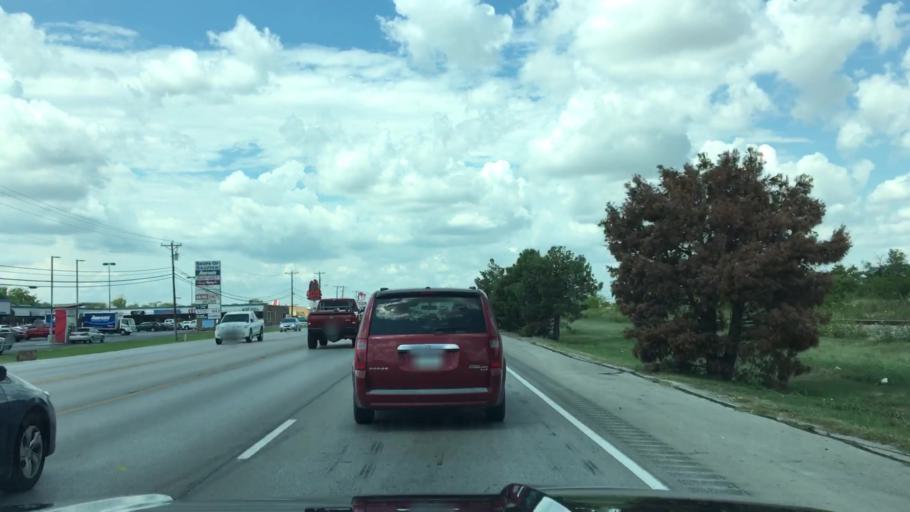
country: US
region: Texas
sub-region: Tarrant County
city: Saginaw
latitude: 32.8752
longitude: -97.3767
